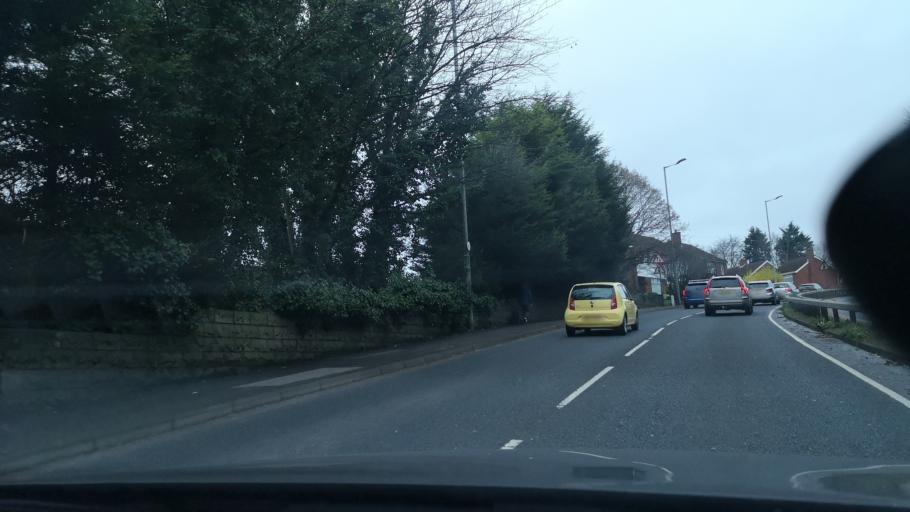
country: GB
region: Northern Ireland
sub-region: Castlereagh District
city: Castlereagh
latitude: 54.5843
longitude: -5.8633
